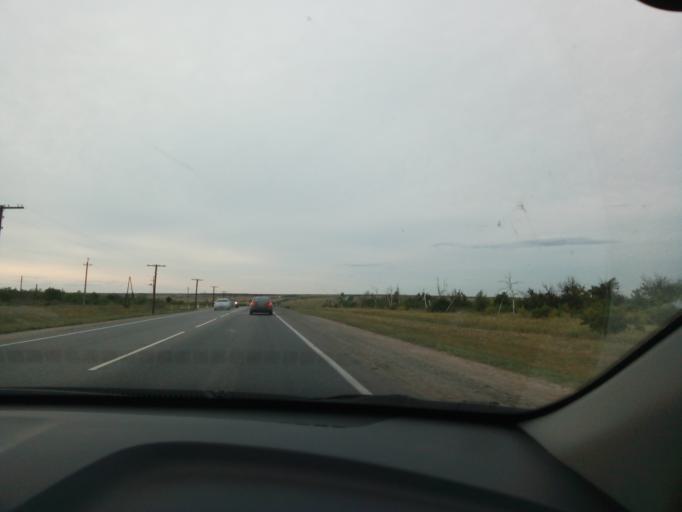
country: RU
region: Volgograd
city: Dubovka
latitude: 49.1171
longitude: 44.8126
